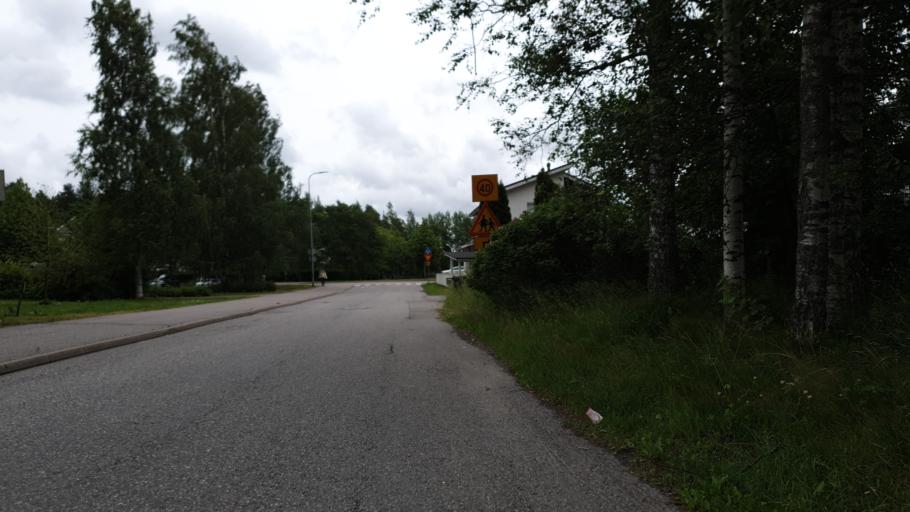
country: FI
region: Uusimaa
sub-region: Helsinki
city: Helsinki
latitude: 60.2836
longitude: 24.9069
